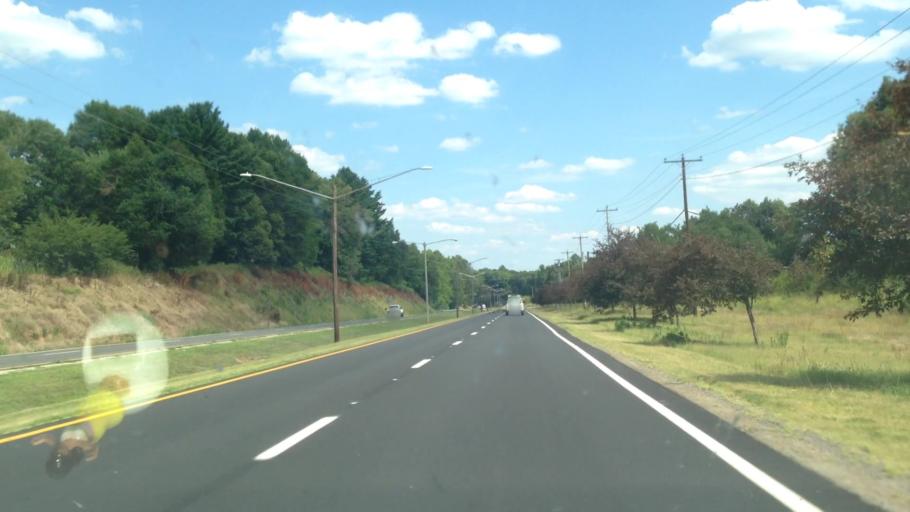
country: US
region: Virginia
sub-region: City of Danville
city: Danville
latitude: 36.5843
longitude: -79.4459
